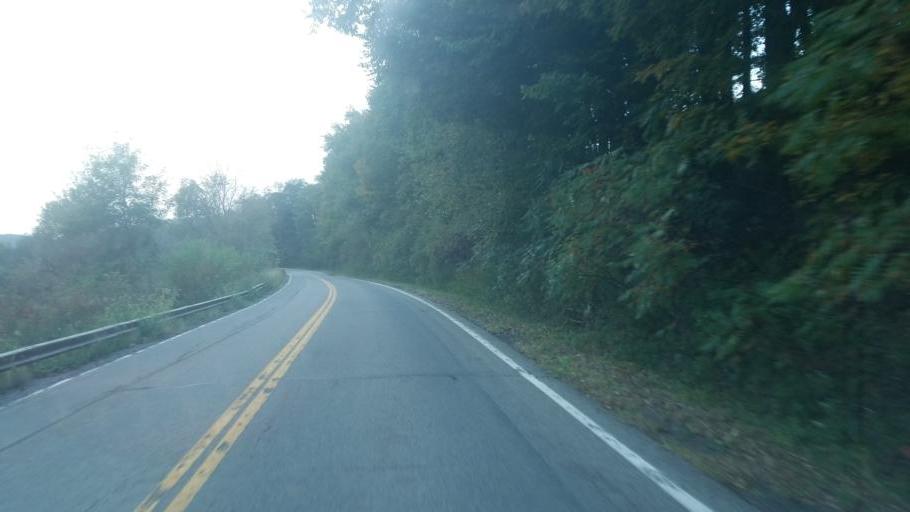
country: US
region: New York
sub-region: Allegany County
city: Cuba
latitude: 42.1810
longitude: -78.3690
